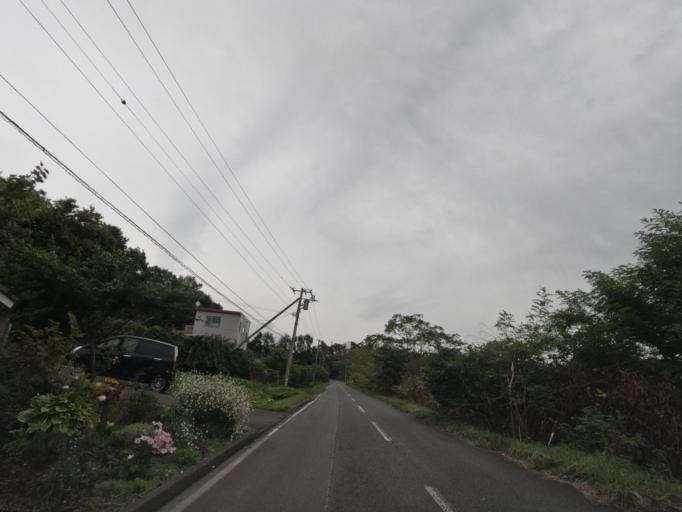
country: JP
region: Hokkaido
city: Date
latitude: 42.4037
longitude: 140.9136
